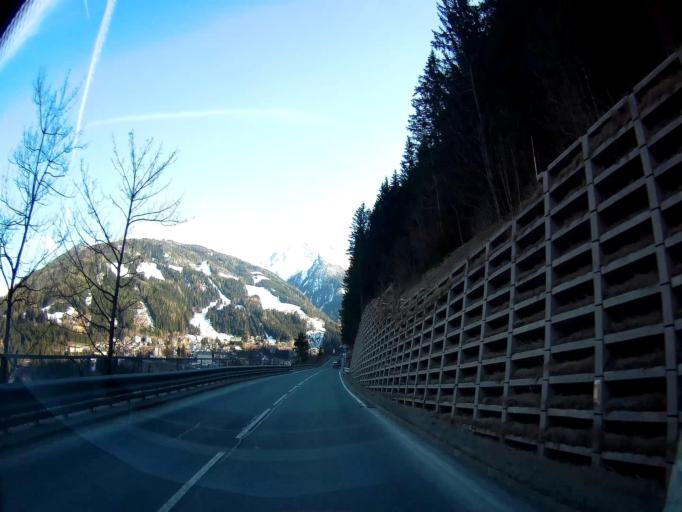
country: AT
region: Salzburg
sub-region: Politischer Bezirk Sankt Johann im Pongau
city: Bad Gastein
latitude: 47.1301
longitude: 13.1297
